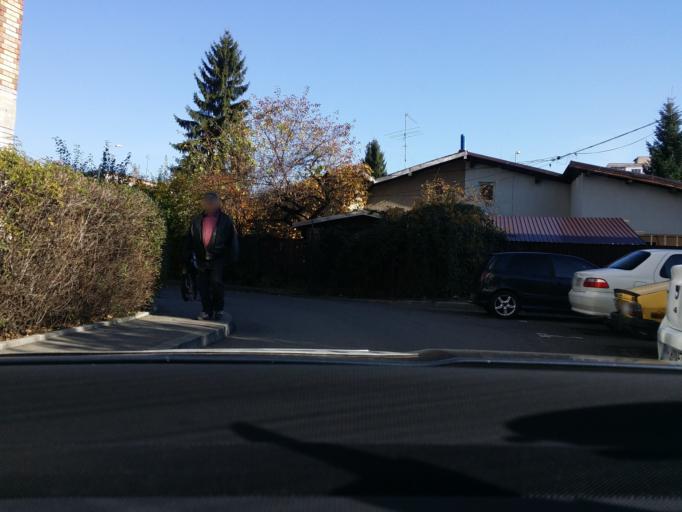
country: RO
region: Prahova
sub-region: Municipiul Campina
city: Campina
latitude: 45.1192
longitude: 25.7389
